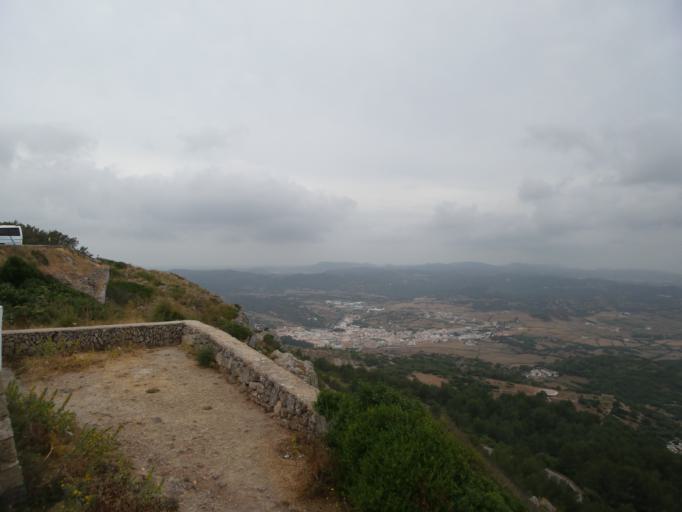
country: ES
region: Balearic Islands
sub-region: Illes Balears
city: Mercadal
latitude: 39.9855
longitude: 4.1139
